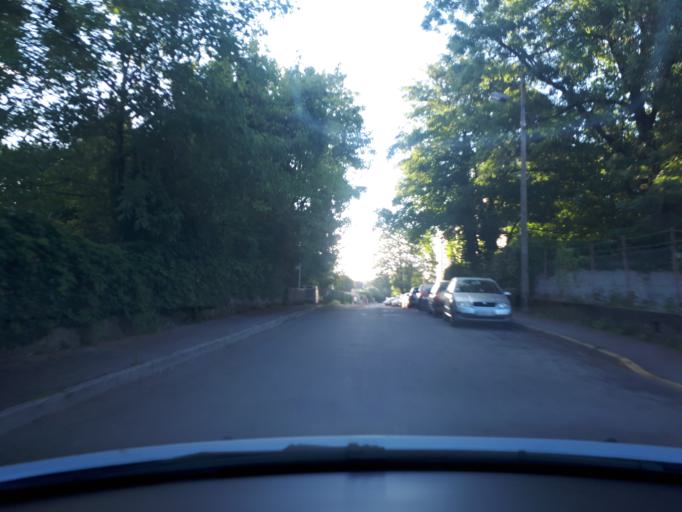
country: FR
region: Rhone-Alpes
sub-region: Departement de l'Isere
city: Bourgoin
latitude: 45.5856
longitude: 5.2835
